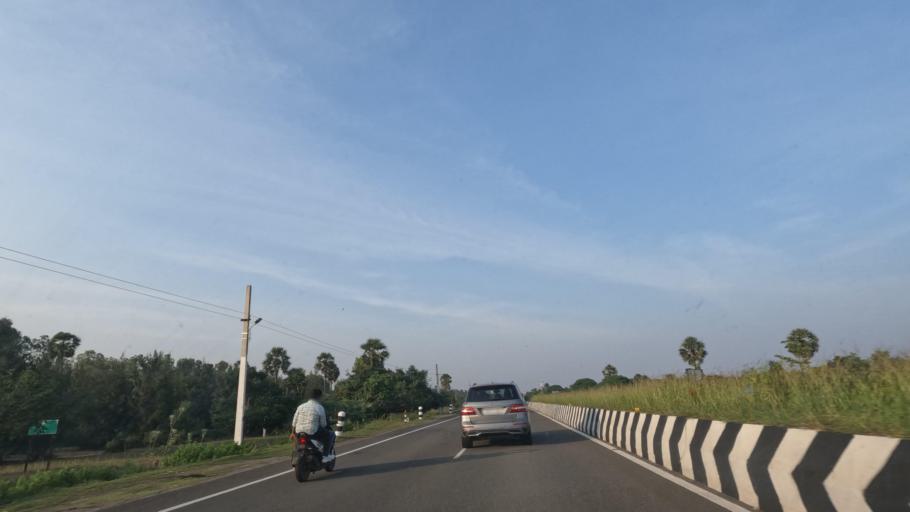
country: IN
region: Tamil Nadu
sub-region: Kancheepuram
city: Mamallapuram
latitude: 12.6768
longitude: 80.2125
